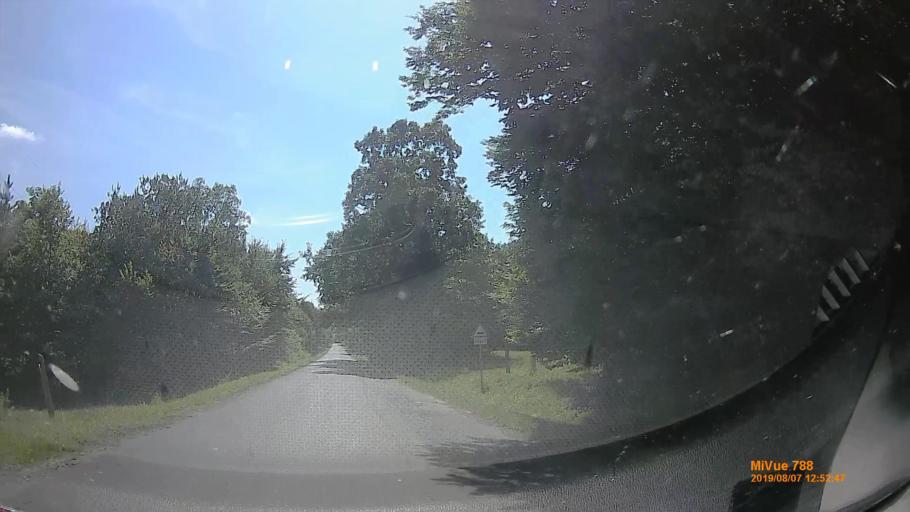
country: HU
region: Zala
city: Cserszegtomaj
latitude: 46.8442
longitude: 17.2674
